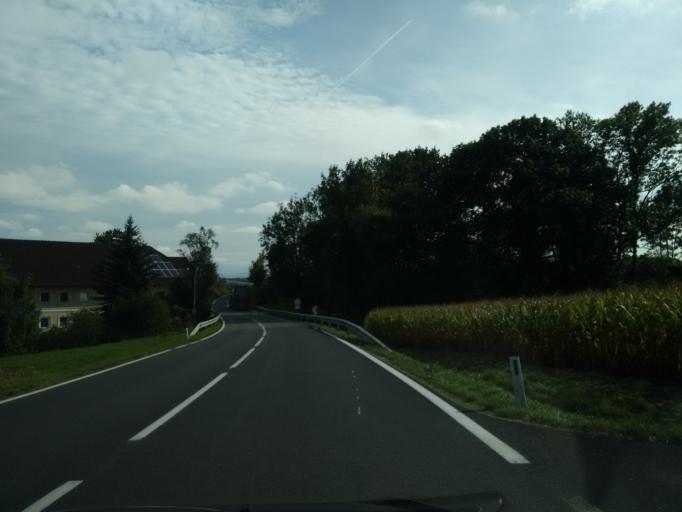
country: AT
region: Upper Austria
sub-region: Politischer Bezirk Steyr-Land
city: Bad Hall
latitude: 48.0989
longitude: 14.1873
